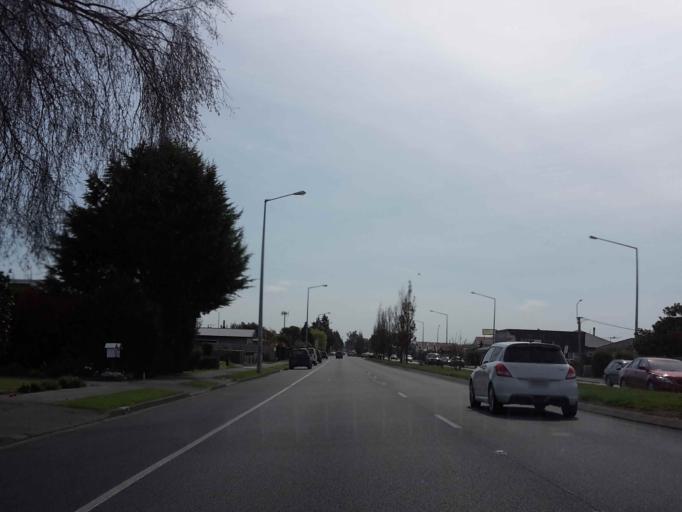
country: NZ
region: Canterbury
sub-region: Waimakariri District
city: Kaiapoi
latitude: -43.4488
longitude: 172.6298
